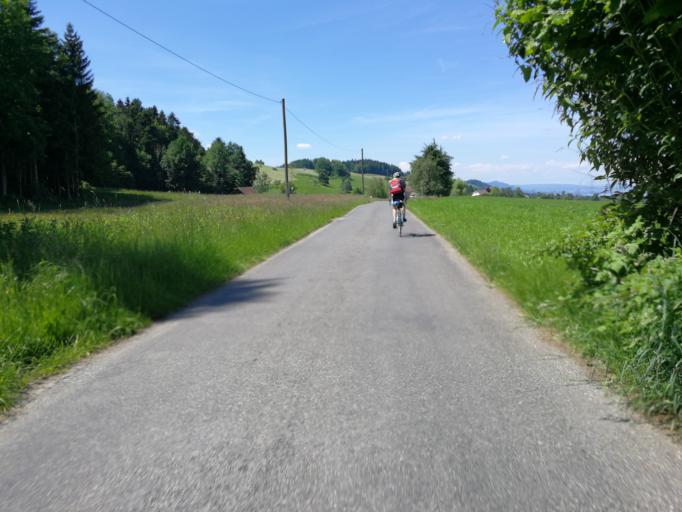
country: CH
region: Zurich
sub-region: Bezirk Horgen
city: Waedenswil / Hangenmoos
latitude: 47.2075
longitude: 8.6421
